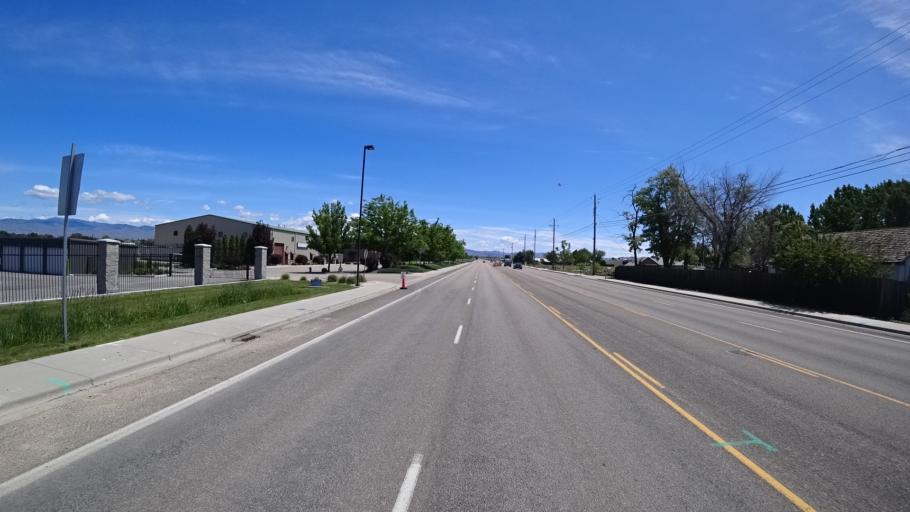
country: US
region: Idaho
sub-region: Ada County
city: Garden City
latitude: 43.5756
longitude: -116.2671
